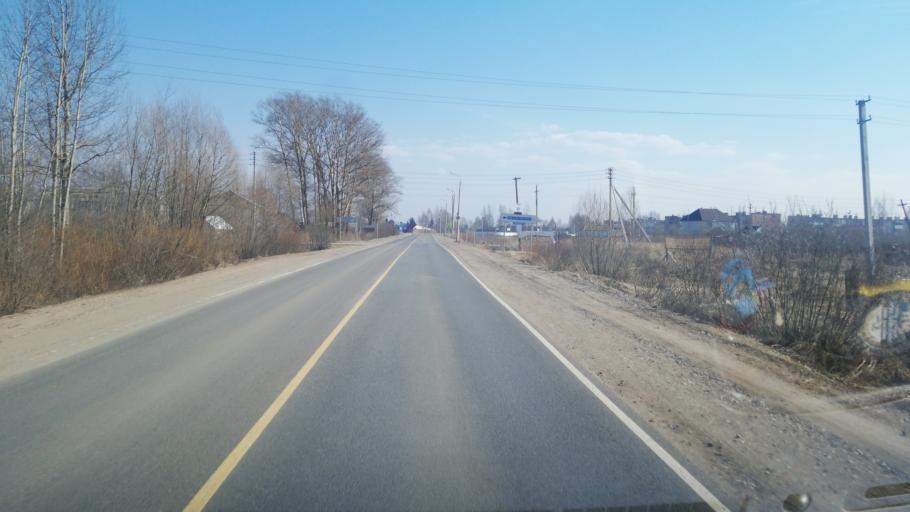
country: RU
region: Jaroslavl
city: Semibratovo
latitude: 57.2339
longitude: 39.4911
